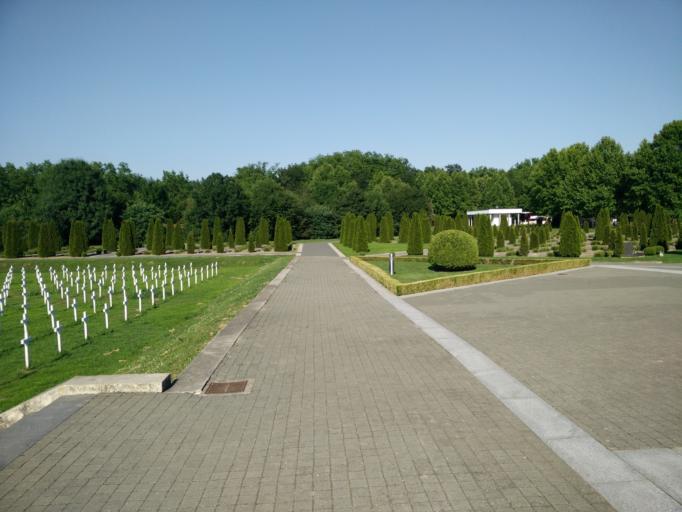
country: HR
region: Vukovarsko-Srijemska
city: Vukovar
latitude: 45.3278
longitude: 19.0389
